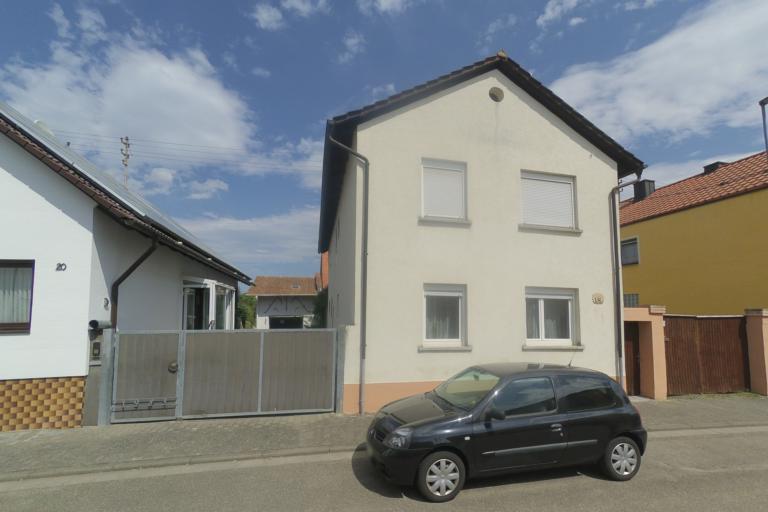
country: DE
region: Rheinland-Pfalz
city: Frankenthal
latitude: 49.5164
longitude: 8.3318
